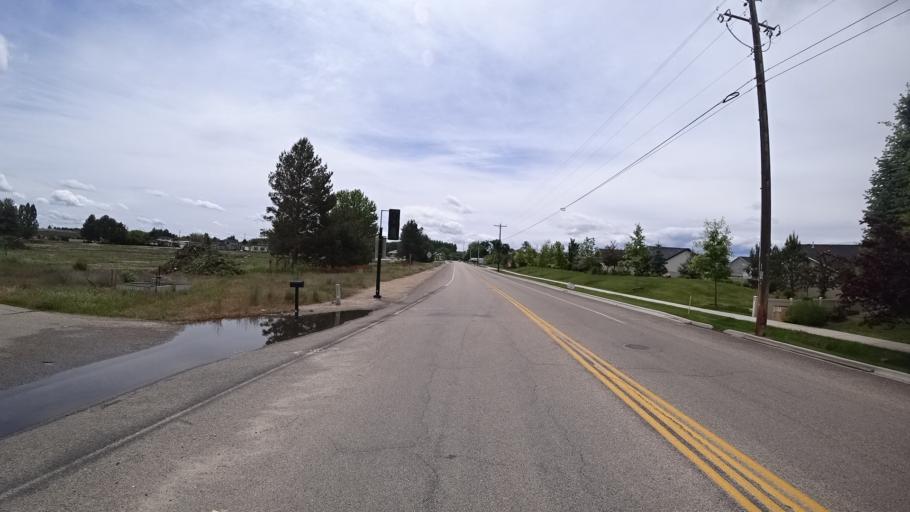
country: US
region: Idaho
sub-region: Ada County
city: Eagle
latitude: 43.6992
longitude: -116.4036
